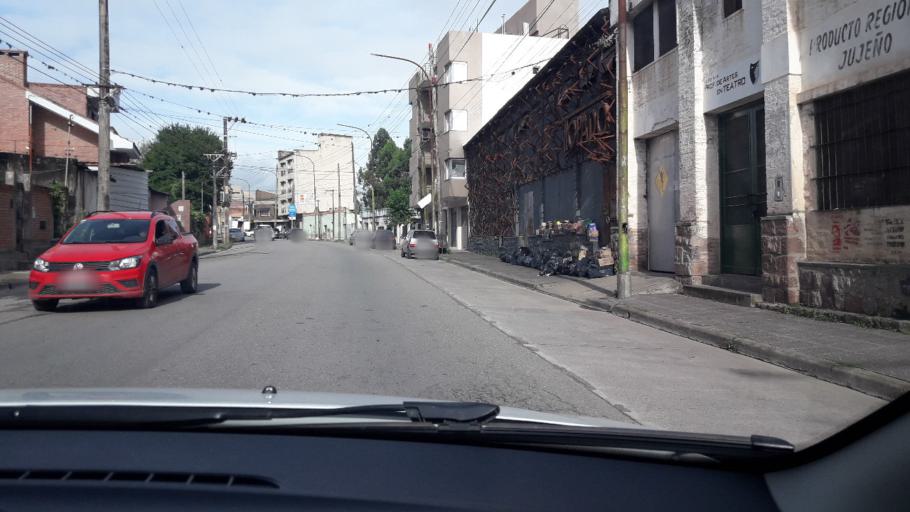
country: AR
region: Jujuy
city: San Salvador de Jujuy
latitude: -24.1788
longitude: -65.3307
